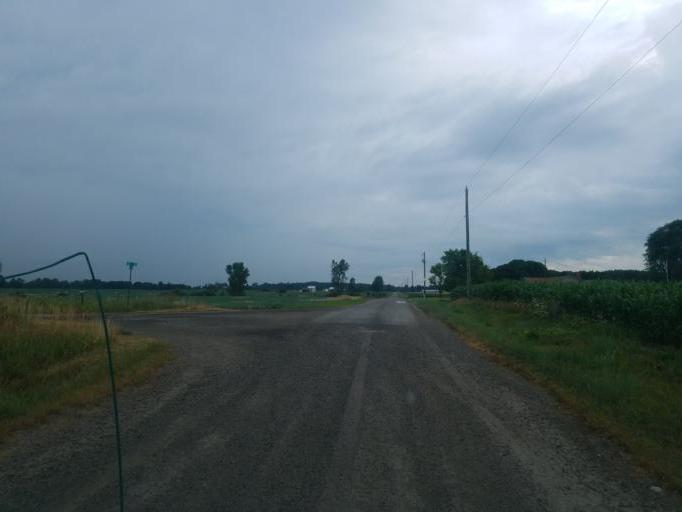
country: US
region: Ohio
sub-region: Defiance County
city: Hicksville
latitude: 41.3508
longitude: -84.8040
